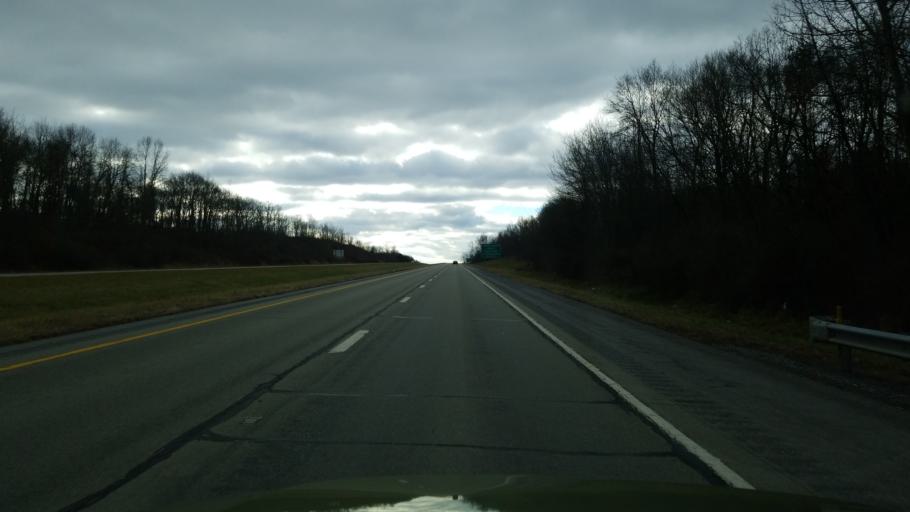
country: US
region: Pennsylvania
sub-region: Indiana County
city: Chevy Chase Heights
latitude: 40.6530
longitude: -79.1161
